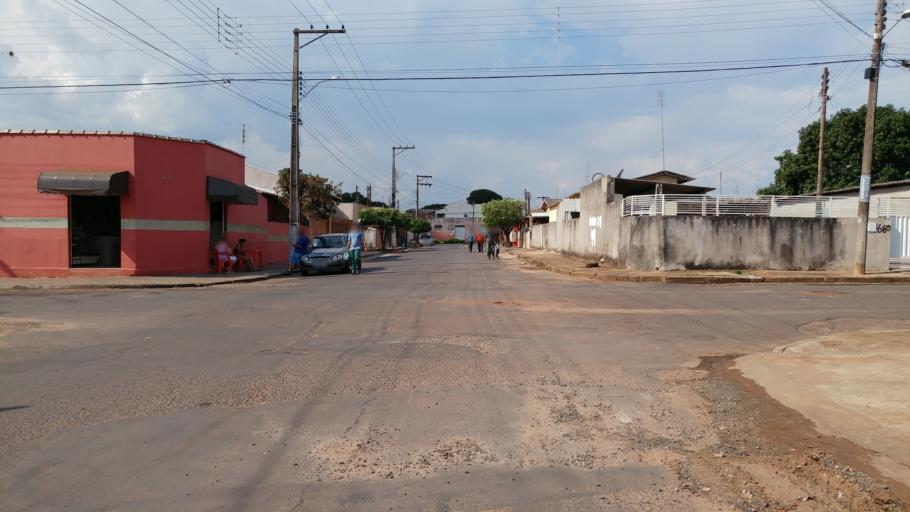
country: BR
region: Sao Paulo
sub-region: Paraguacu Paulista
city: Paraguacu Paulista
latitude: -22.4220
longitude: -50.5863
